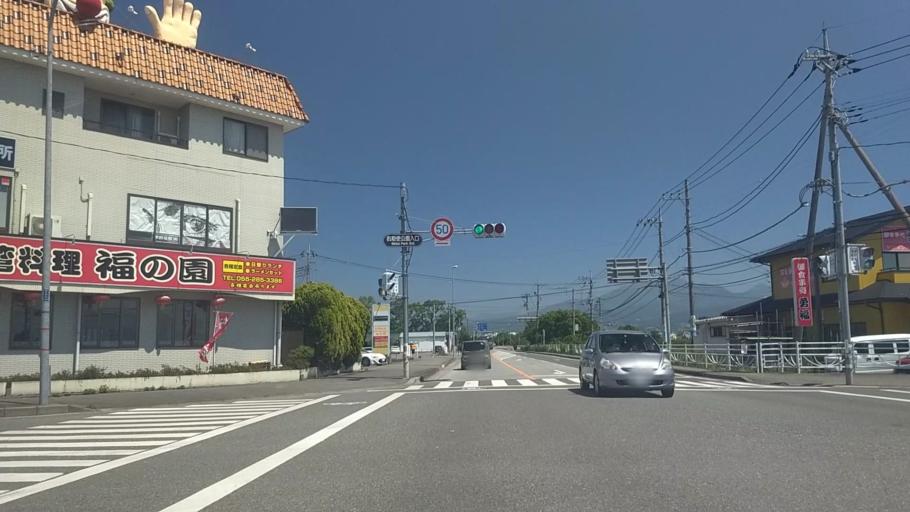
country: JP
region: Yamanashi
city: Nirasaki
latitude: 35.6690
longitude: 138.4647
